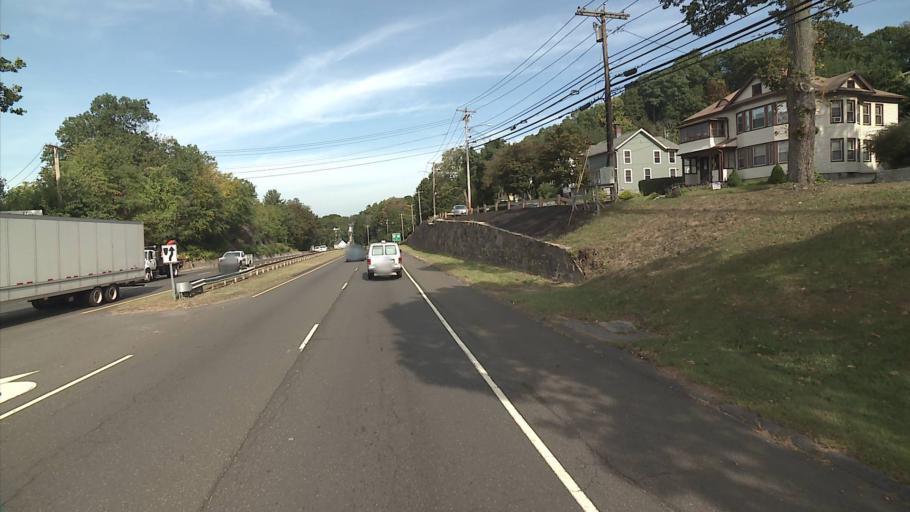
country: US
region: Connecticut
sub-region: New Haven County
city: Derby
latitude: 41.3109
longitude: -73.0760
